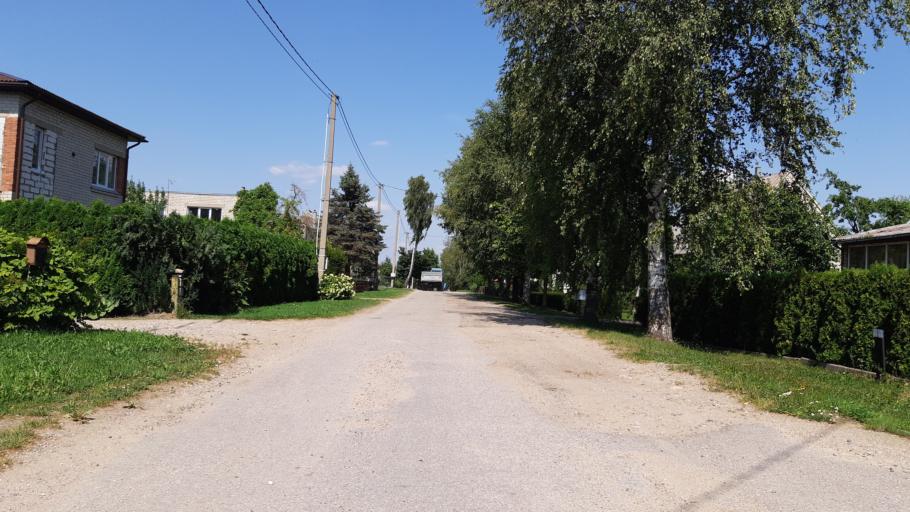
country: LT
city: Virbalis
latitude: 54.6211
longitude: 22.8166
